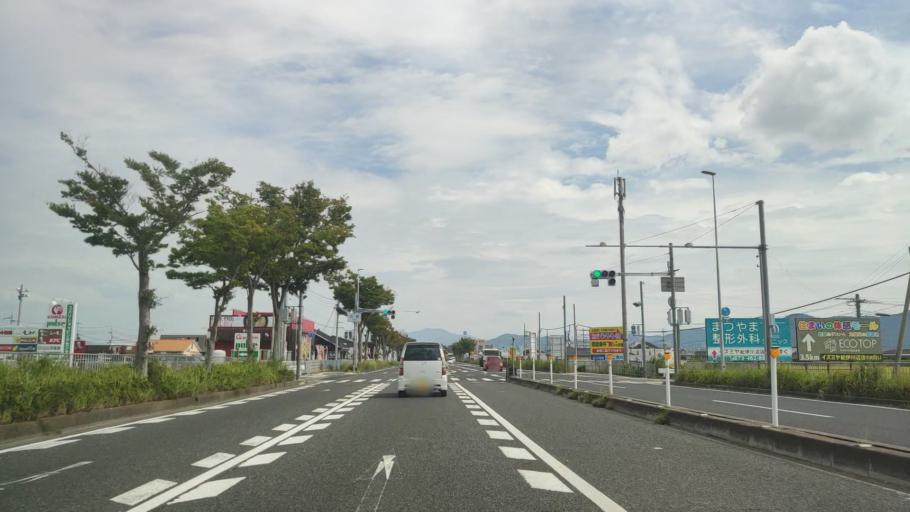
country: JP
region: Wakayama
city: Wakayama-shi
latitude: 34.2564
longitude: 135.2249
